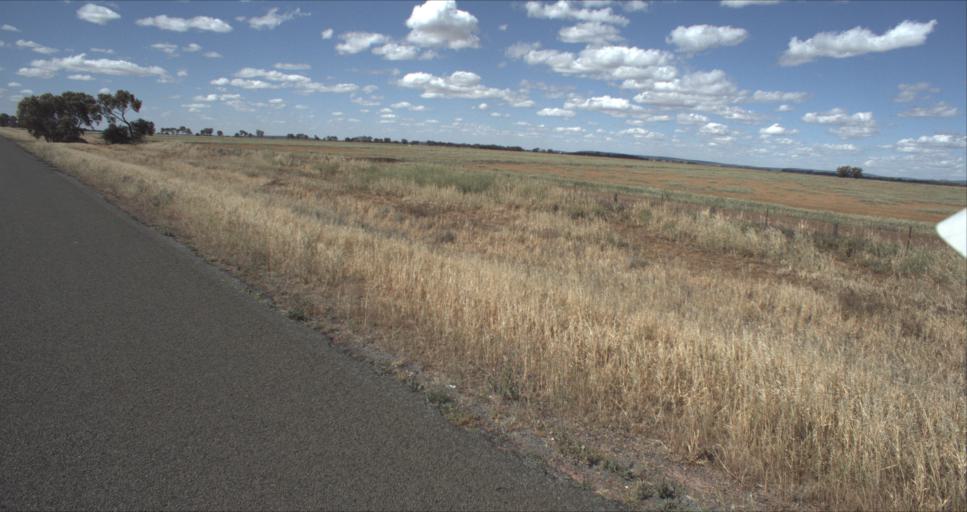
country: AU
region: New South Wales
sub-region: Leeton
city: Leeton
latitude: -34.4692
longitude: 146.2512
